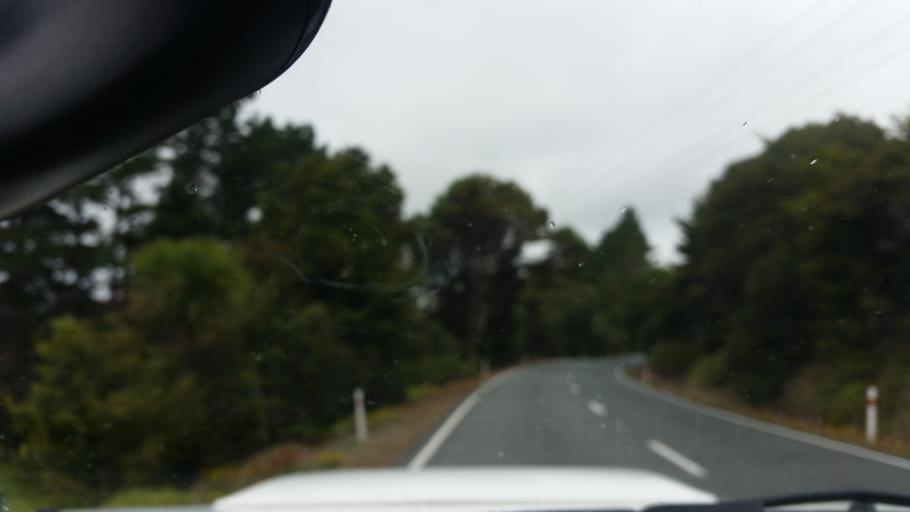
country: NZ
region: Auckland
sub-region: Auckland
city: Wellsford
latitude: -36.1321
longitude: 174.5439
